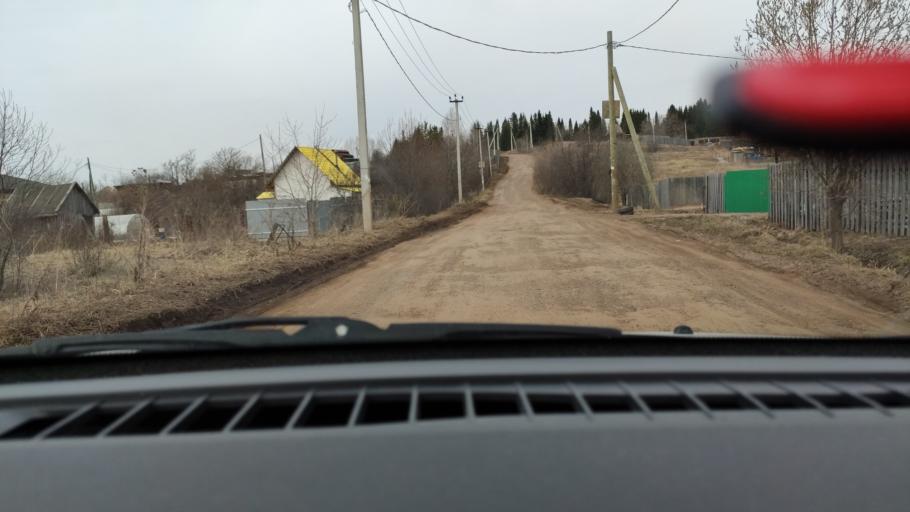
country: RU
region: Perm
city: Kultayevo
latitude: 57.8967
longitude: 56.0148
